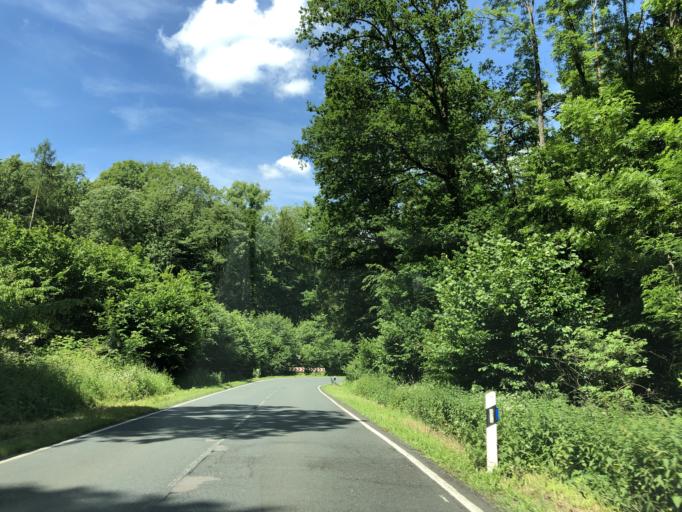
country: DE
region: Hesse
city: Wetter
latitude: 50.8433
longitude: 8.6848
